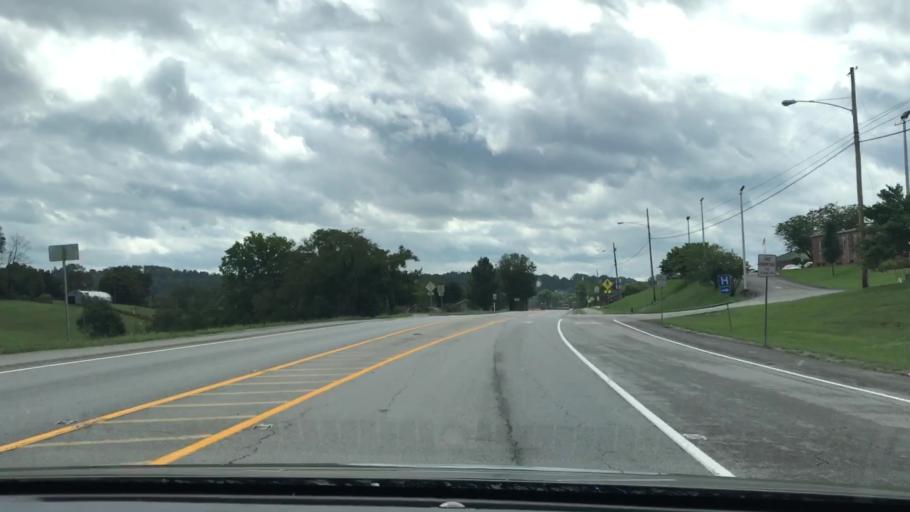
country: US
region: Kentucky
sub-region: Cumberland County
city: Burkesville
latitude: 36.7974
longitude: -85.3729
